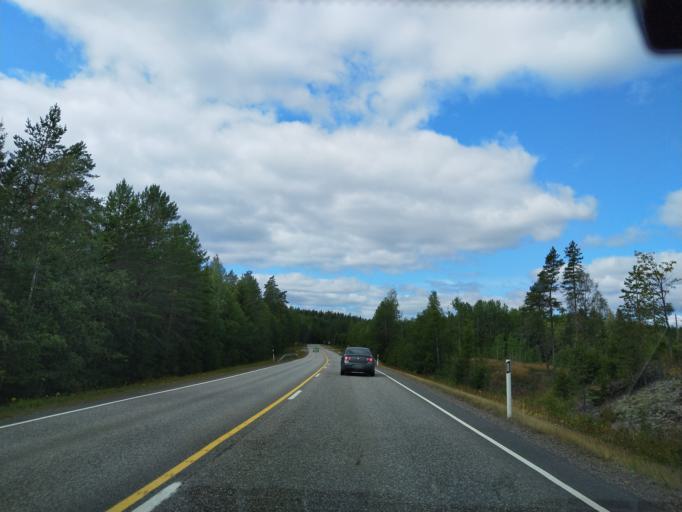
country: FI
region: Haeme
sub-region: Riihimaeki
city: Loppi
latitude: 60.7373
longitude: 24.3755
